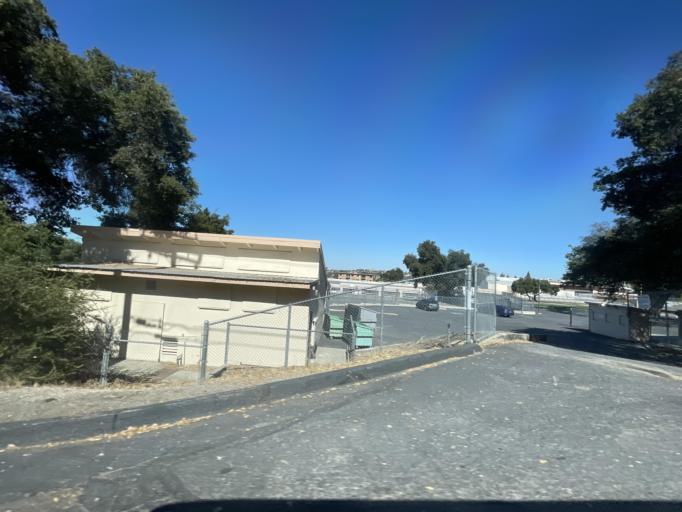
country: US
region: California
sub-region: San Luis Obispo County
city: Paso Robles
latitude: 35.6409
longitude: -120.6951
